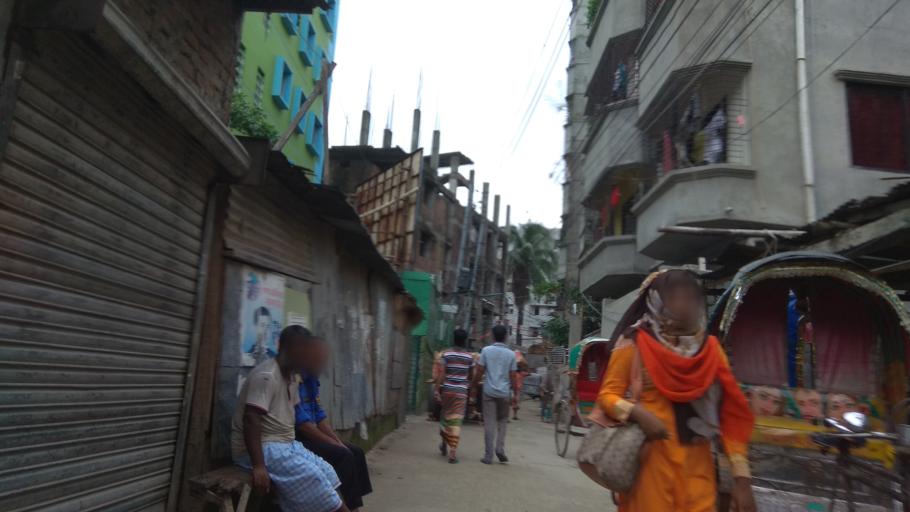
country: BD
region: Dhaka
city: Azimpur
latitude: 23.7949
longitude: 90.3860
